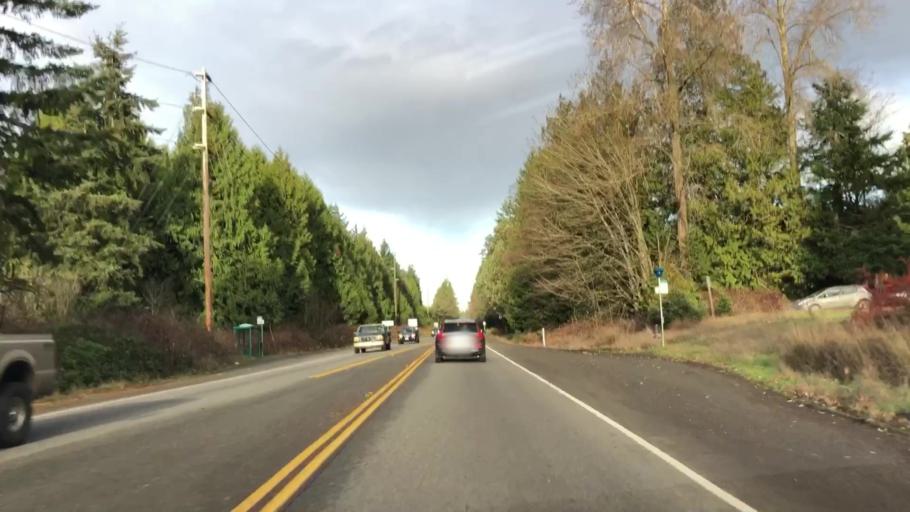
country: US
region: Washington
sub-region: Kitsap County
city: Suquamish
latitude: 47.6800
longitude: -122.5398
